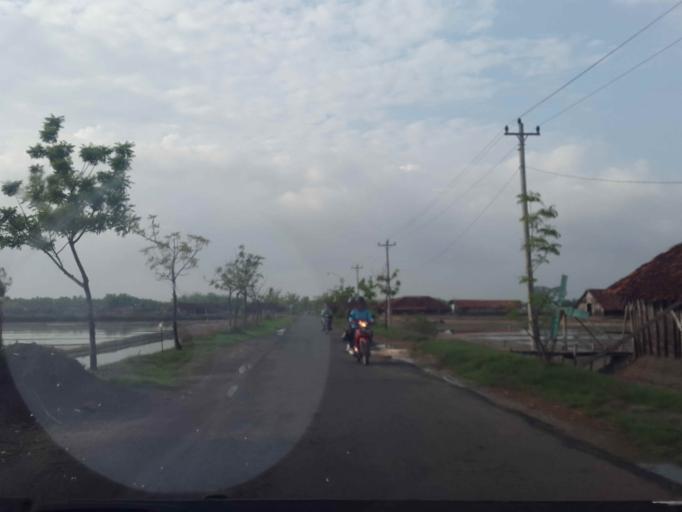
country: ID
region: Central Java
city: Dresi Kulon
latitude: -6.7020
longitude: 111.2696
